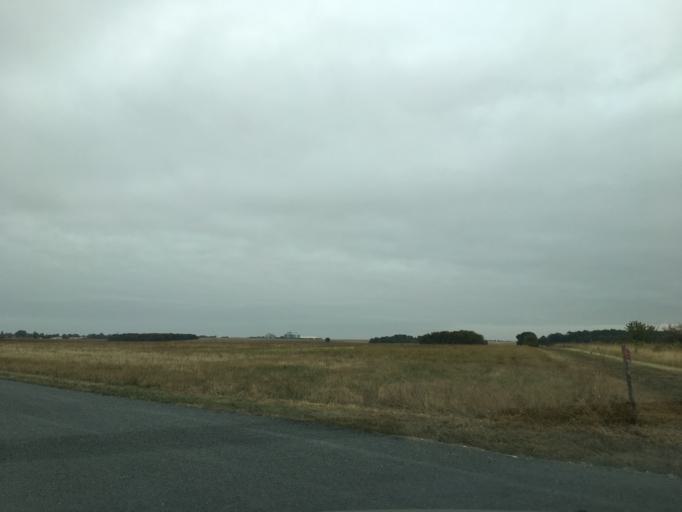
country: FR
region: Poitou-Charentes
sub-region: Departement des Deux-Sevres
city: Beauvoir-sur-Niort
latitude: 46.0842
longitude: -0.4910
